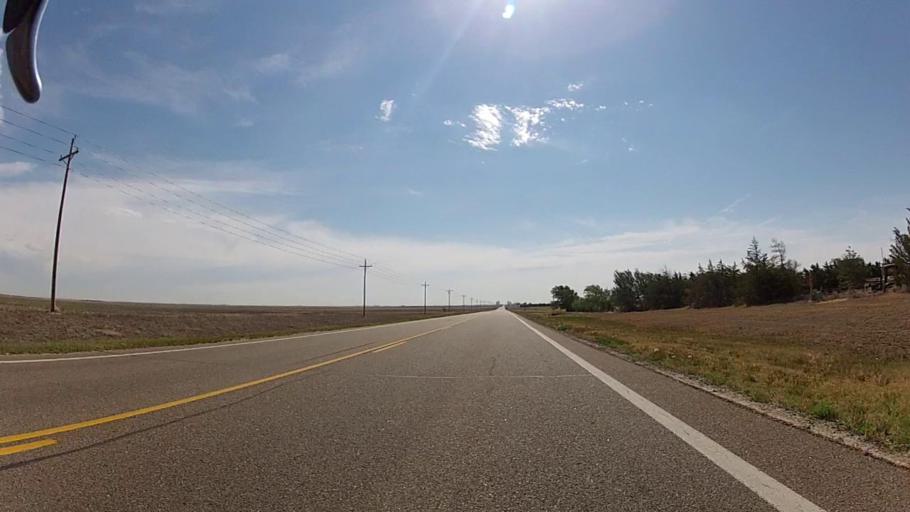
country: US
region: Kansas
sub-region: Grant County
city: Ulysses
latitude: 37.5619
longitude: -101.2929
